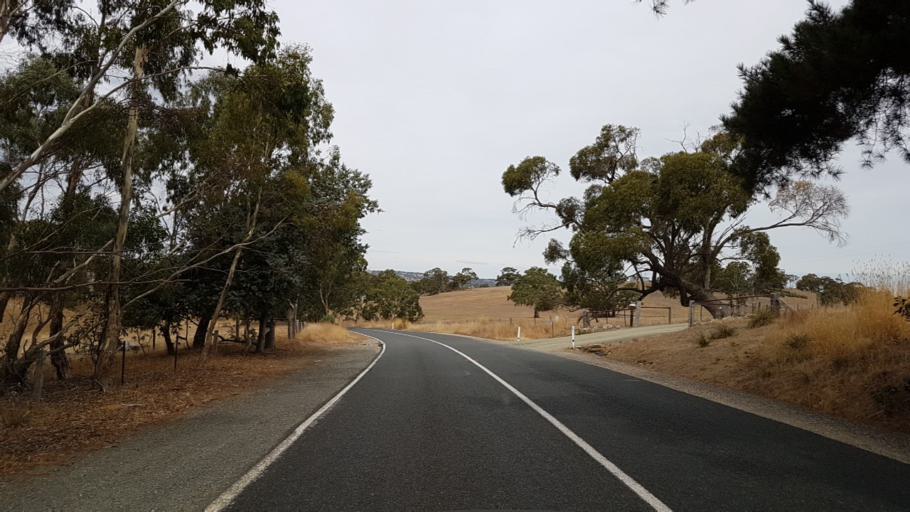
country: AU
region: South Australia
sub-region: Adelaide Hills
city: Birdwood
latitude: -34.7862
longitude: 138.9387
